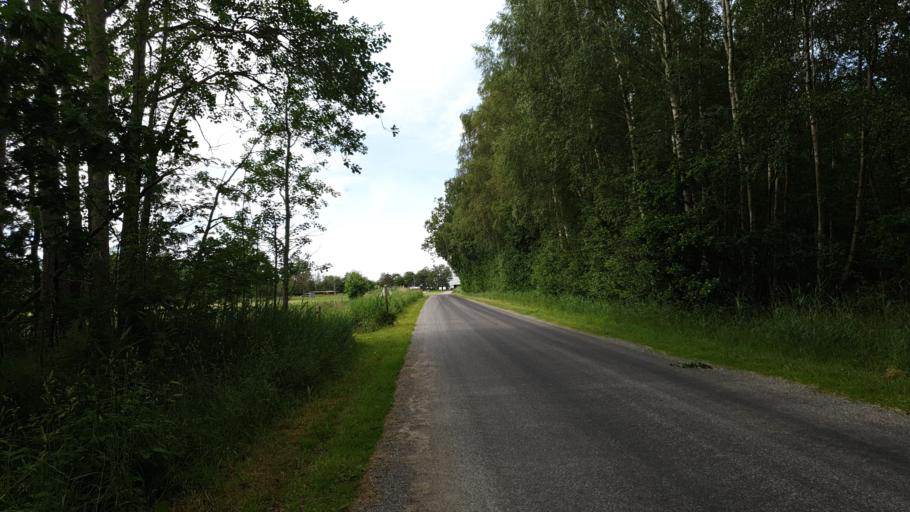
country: DK
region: North Denmark
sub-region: Laeso Kommune
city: Byrum
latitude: 57.2496
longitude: 10.9863
